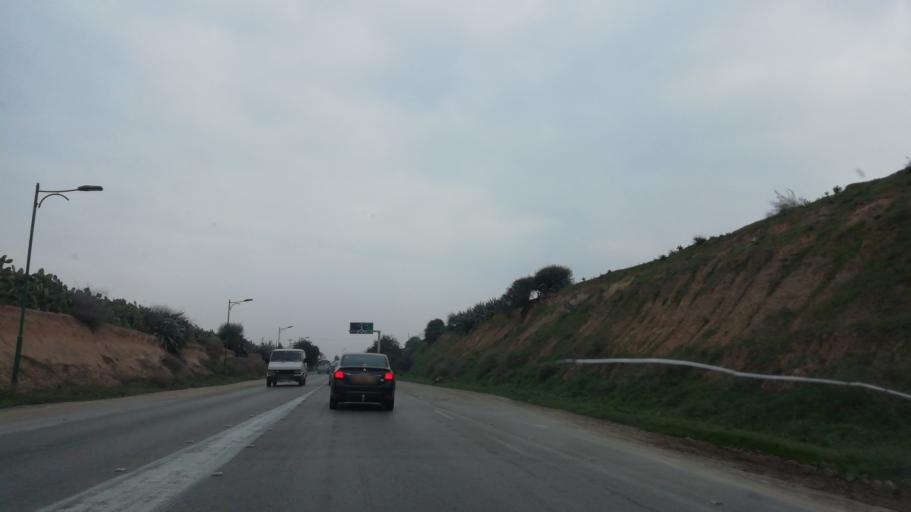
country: DZ
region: Mascara
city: Sig
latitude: 35.5530
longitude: -0.2526
